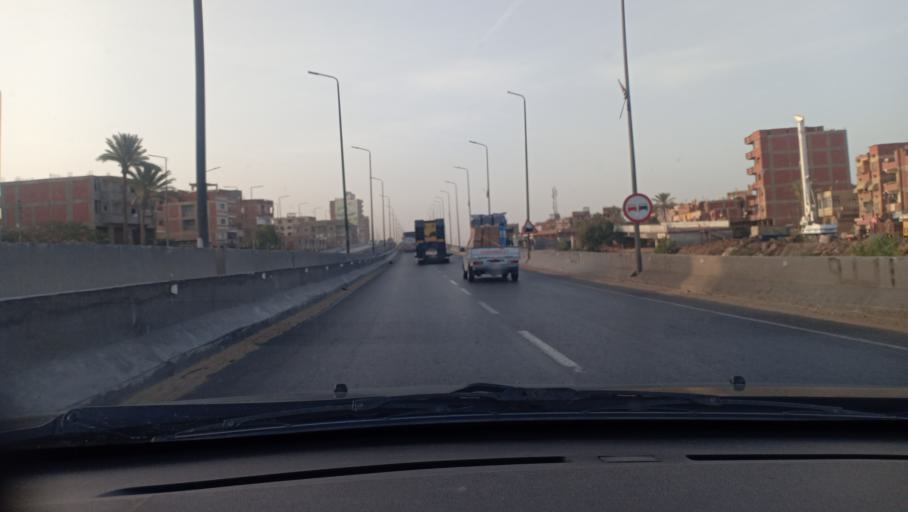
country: EG
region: Muhafazat al Minufiyah
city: Quwaysina
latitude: 30.5454
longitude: 31.2693
